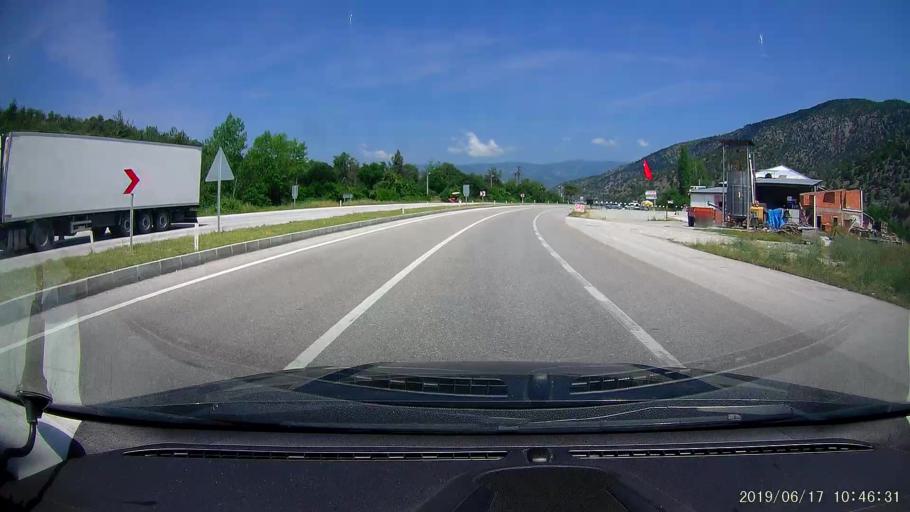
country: TR
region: Corum
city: Hacihamza
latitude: 41.0685
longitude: 34.4604
